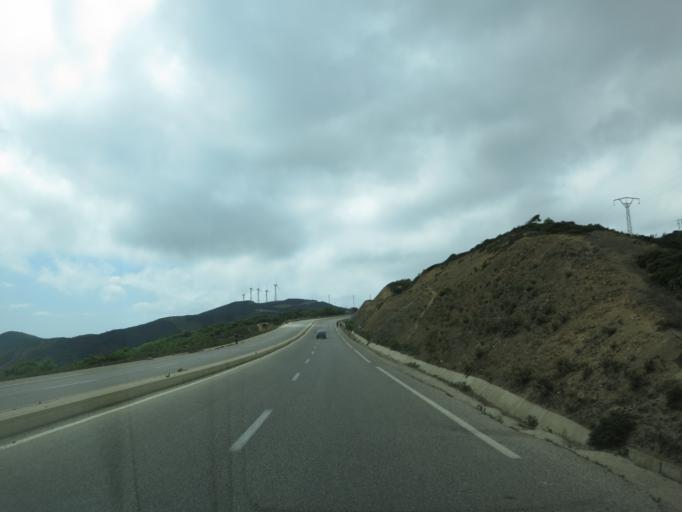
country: ES
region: Ceuta
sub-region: Ceuta
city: Ceuta
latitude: 35.8623
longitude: -5.4222
